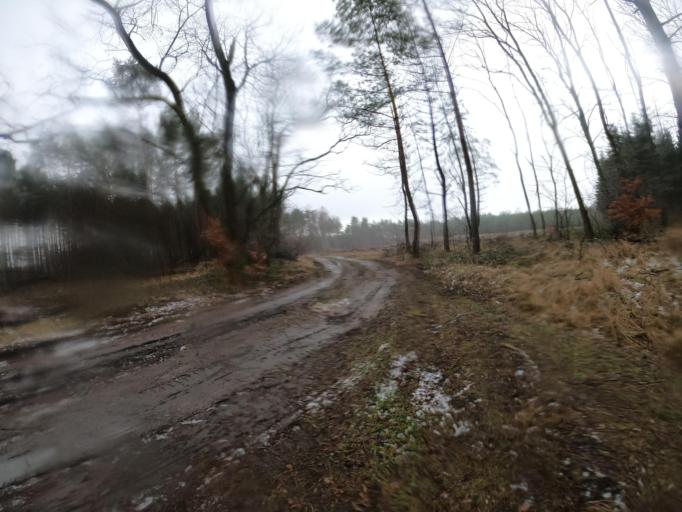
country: PL
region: Lubusz
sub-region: Powiat slubicki
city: Cybinka
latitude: 52.1817
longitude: 14.8704
